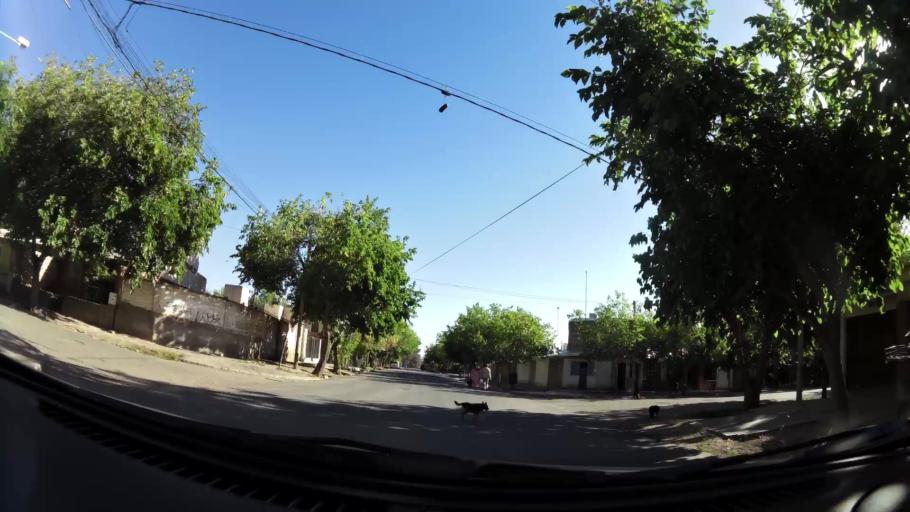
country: AR
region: Mendoza
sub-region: Departamento de Godoy Cruz
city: Godoy Cruz
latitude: -32.9279
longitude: -68.8669
